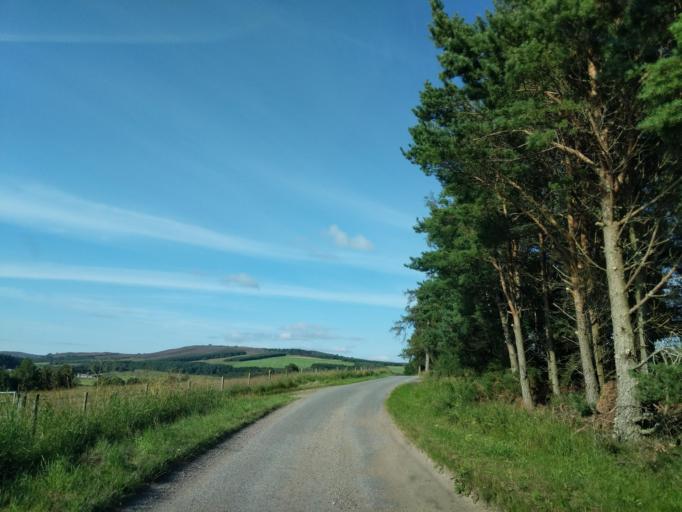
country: GB
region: Scotland
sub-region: Highland
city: Grantown on Spey
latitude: 57.2962
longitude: -3.7111
